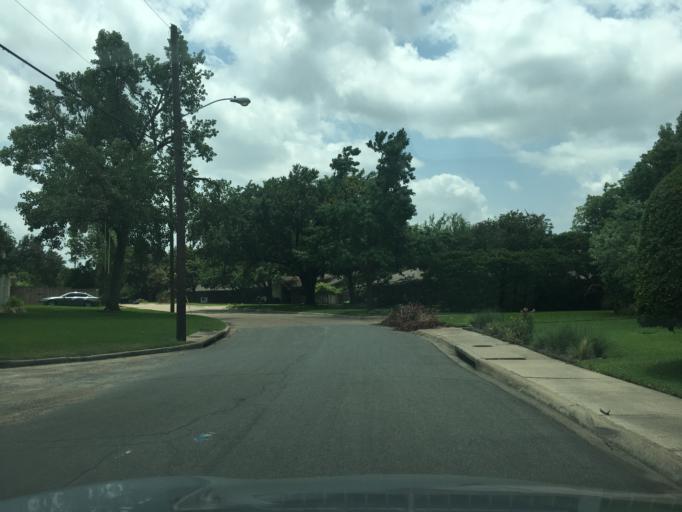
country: US
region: Texas
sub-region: Dallas County
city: Addison
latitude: 32.9014
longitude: -96.8340
